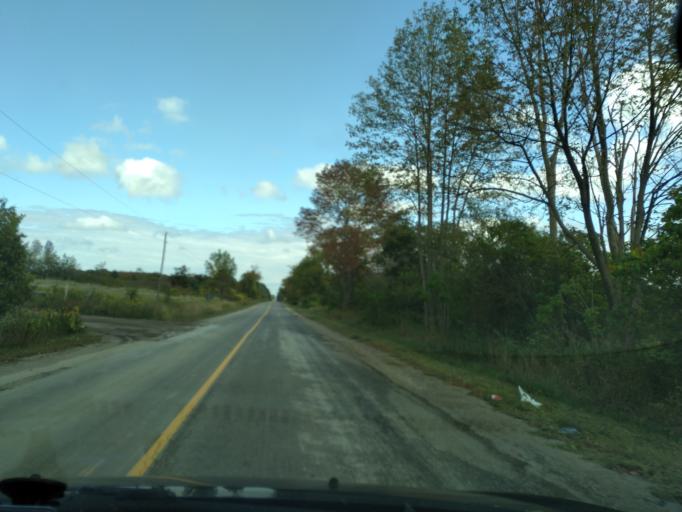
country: CA
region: Ontario
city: Innisfil
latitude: 44.2770
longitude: -79.6042
